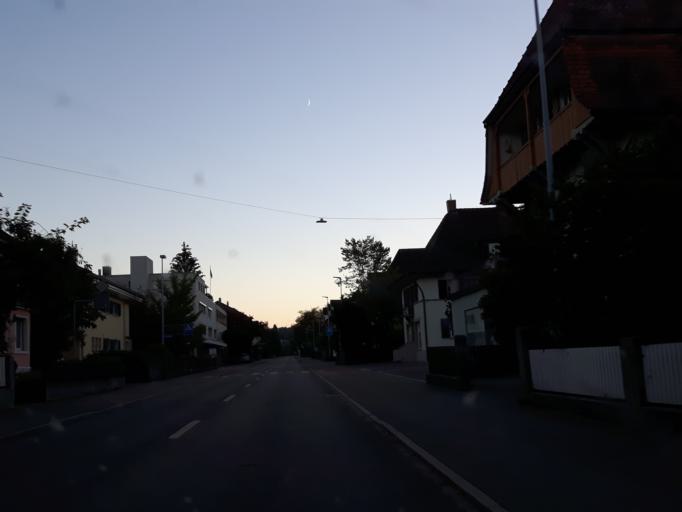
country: CH
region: Bern
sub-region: Oberaargau
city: Langenthal
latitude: 47.2098
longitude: 7.7873
